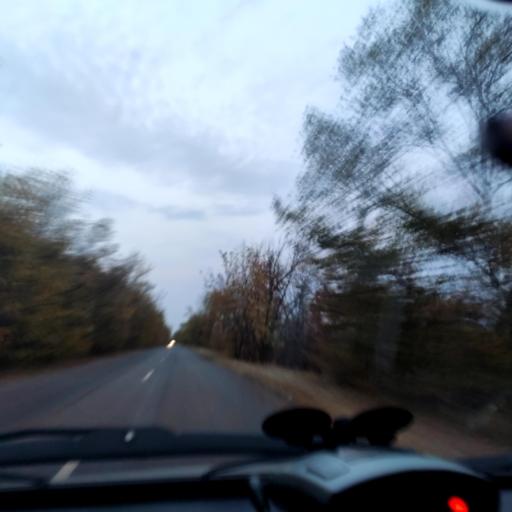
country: RU
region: Voronezj
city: Uryv-Pokrovka
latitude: 51.2159
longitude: 38.8728
